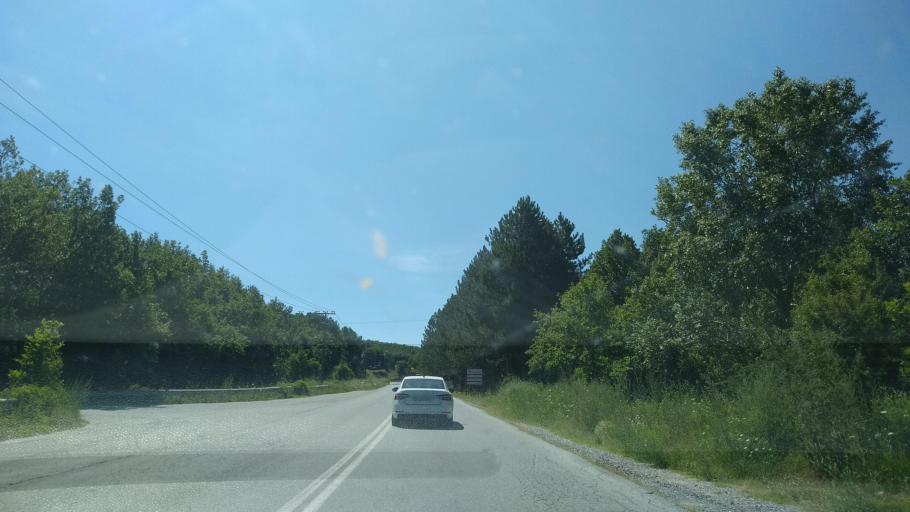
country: GR
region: Central Macedonia
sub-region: Nomos Chalkidikis
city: Megali Panagia
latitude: 40.4608
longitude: 23.6543
